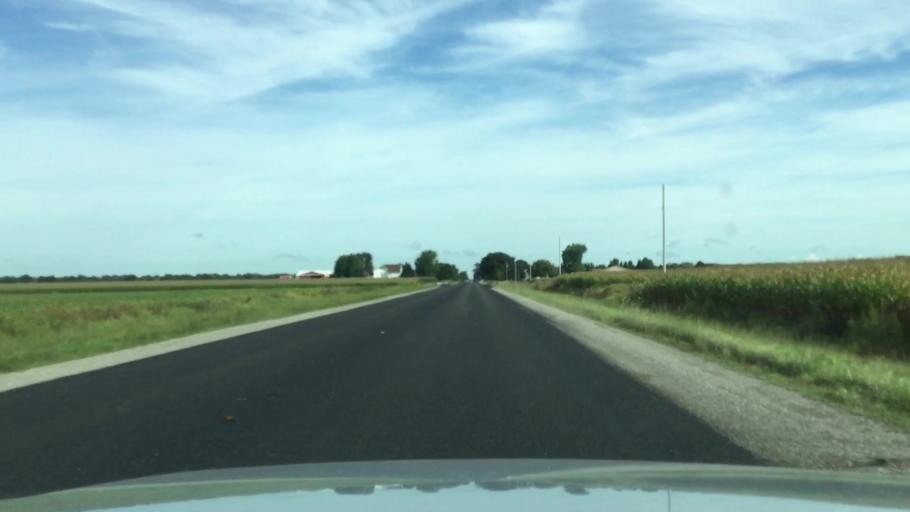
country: US
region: Michigan
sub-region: Genesee County
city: Montrose
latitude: 43.1334
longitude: -83.9291
